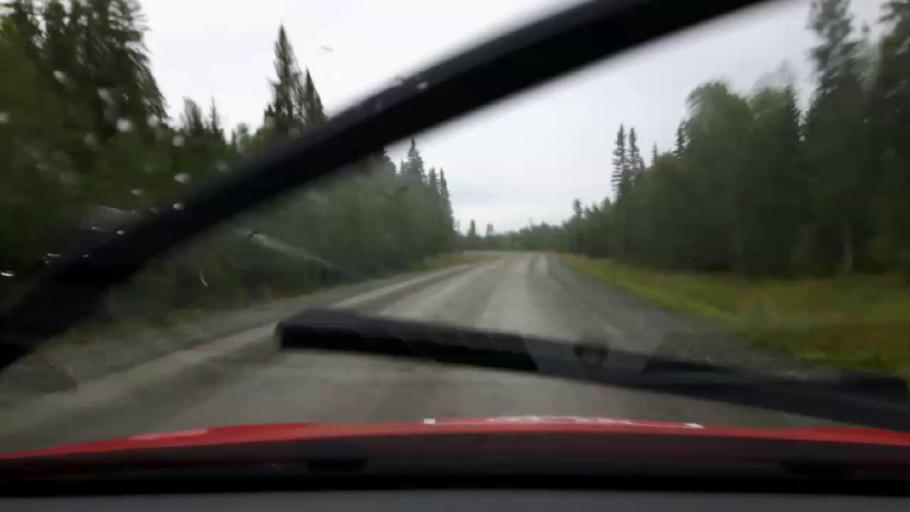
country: SE
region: Jaemtland
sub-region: Are Kommun
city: Are
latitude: 63.4702
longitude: 12.5960
